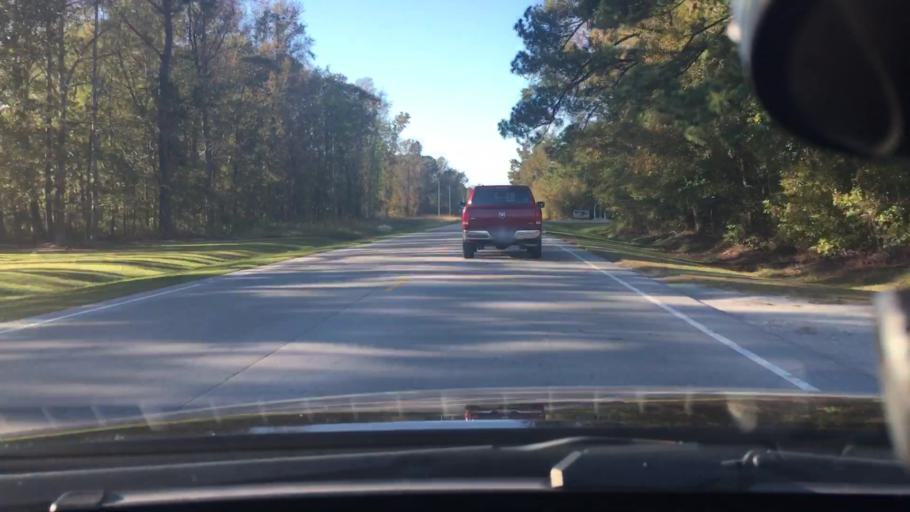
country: US
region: North Carolina
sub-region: Craven County
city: Vanceboro
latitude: 35.2747
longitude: -77.1162
